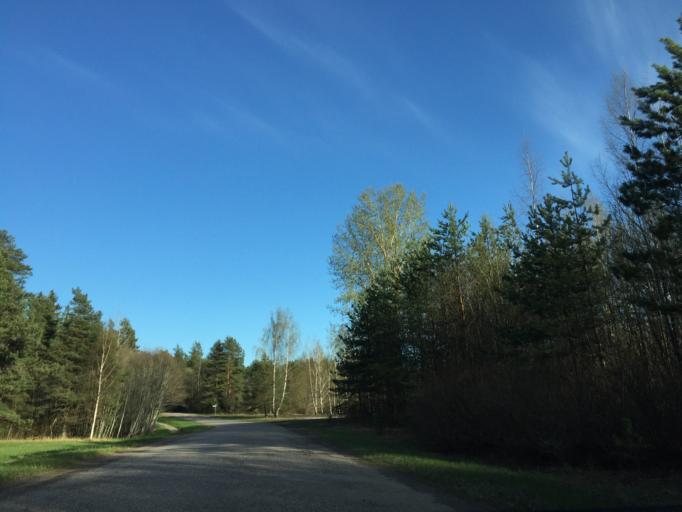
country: LV
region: Valkas Rajons
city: Valka
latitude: 57.7913
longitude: 25.9816
